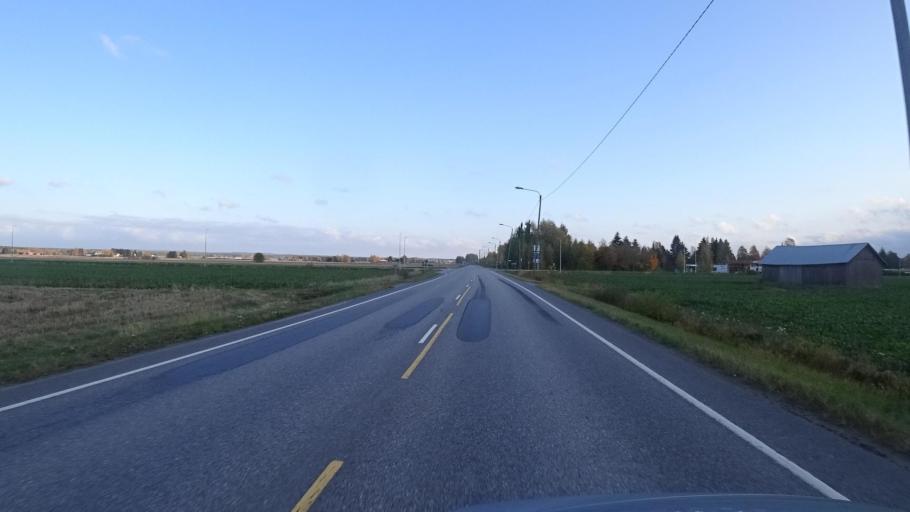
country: FI
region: Satakunta
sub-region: Rauma
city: Saekylae
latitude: 61.0552
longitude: 22.3329
